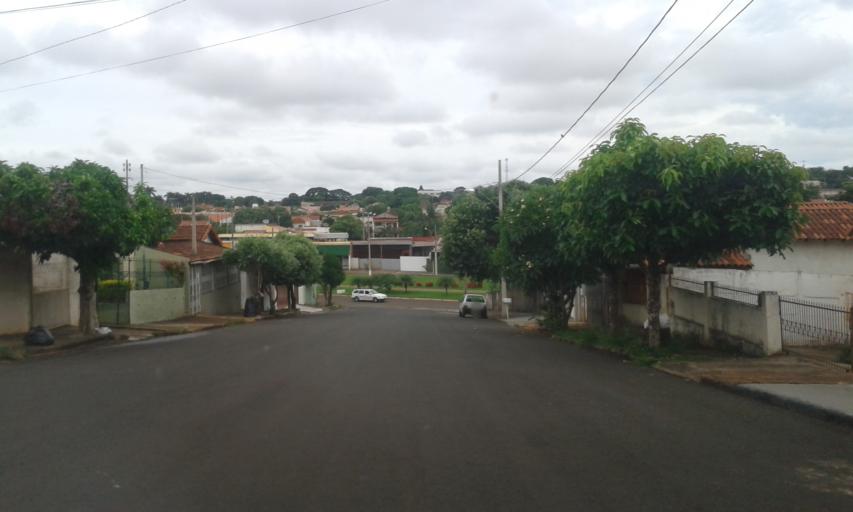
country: BR
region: Minas Gerais
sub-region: Ituiutaba
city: Ituiutaba
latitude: -18.9716
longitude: -49.4538
